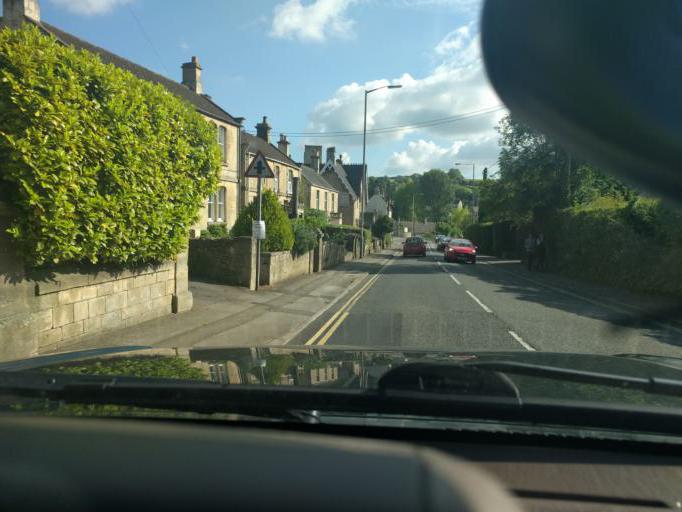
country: GB
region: England
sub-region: Wiltshire
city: Box
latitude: 51.4177
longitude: -2.2498
